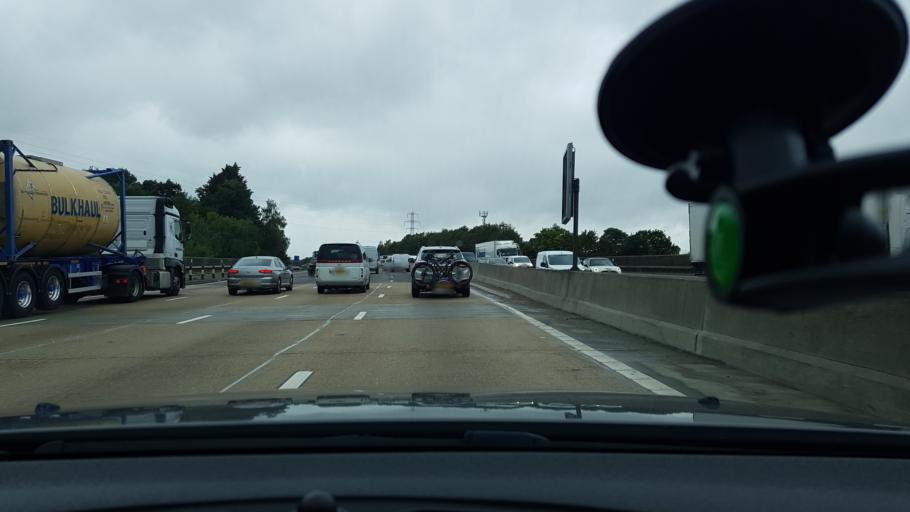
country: GB
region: England
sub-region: Hertfordshire
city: Cuffley
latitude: 51.6914
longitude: -0.1090
